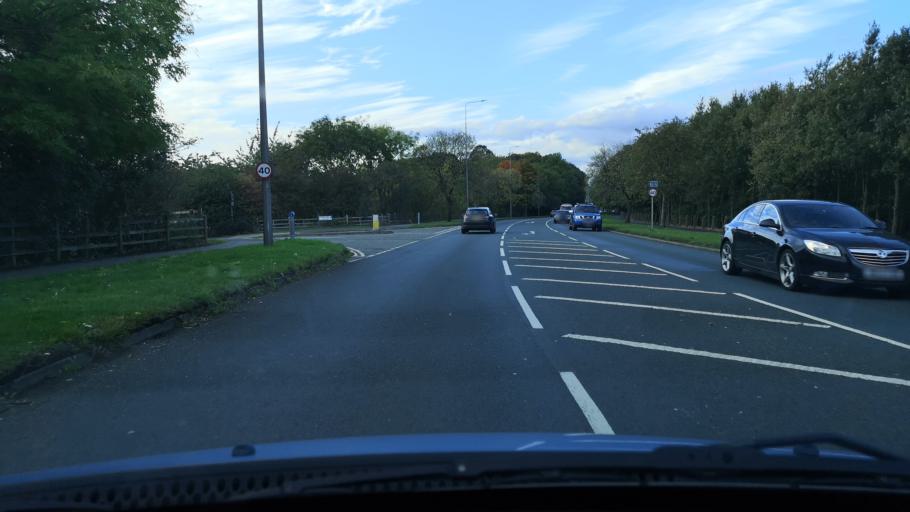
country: GB
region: England
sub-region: North Lincolnshire
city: Scunthorpe
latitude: 53.5806
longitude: -0.6685
